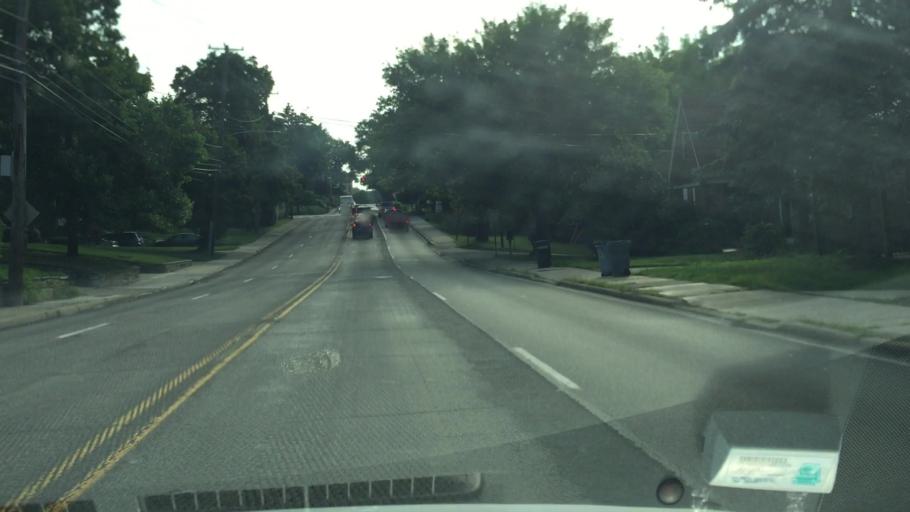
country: US
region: Pennsylvania
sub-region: Allegheny County
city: Dormont
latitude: 40.3845
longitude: -80.0552
